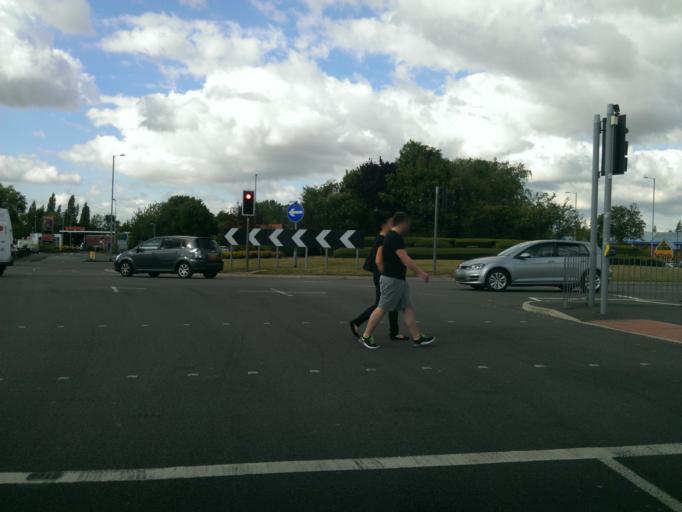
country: GB
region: England
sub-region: Staffordshire
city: Tamworth
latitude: 52.6263
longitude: -1.7046
